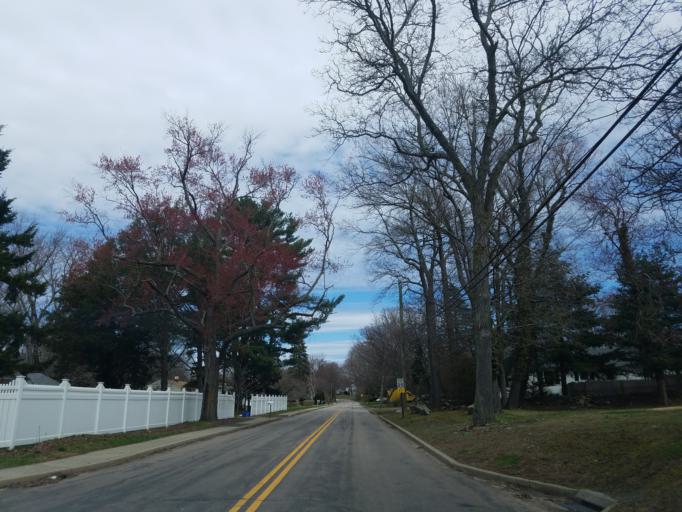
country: US
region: Connecticut
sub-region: Fairfield County
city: Bridgeport
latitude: 41.1824
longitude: -73.2452
